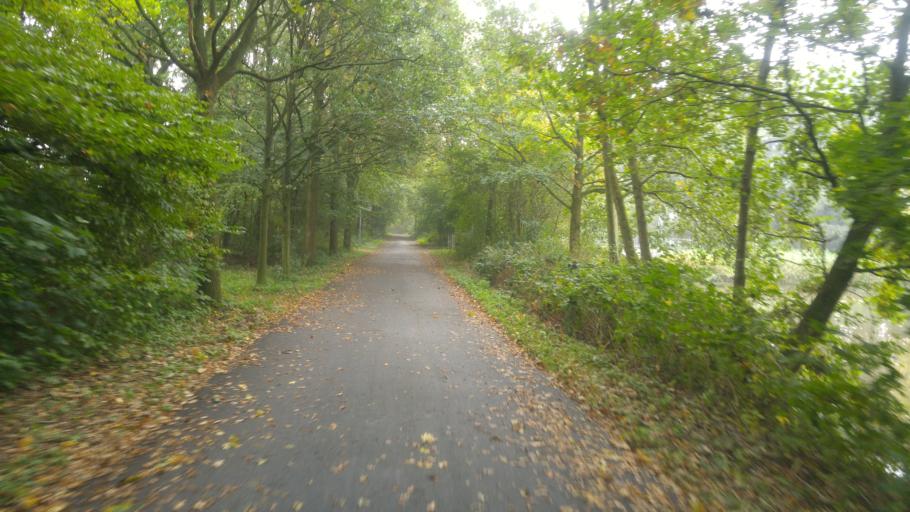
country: DE
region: Bremen
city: Bremen
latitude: 53.1110
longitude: 8.8240
